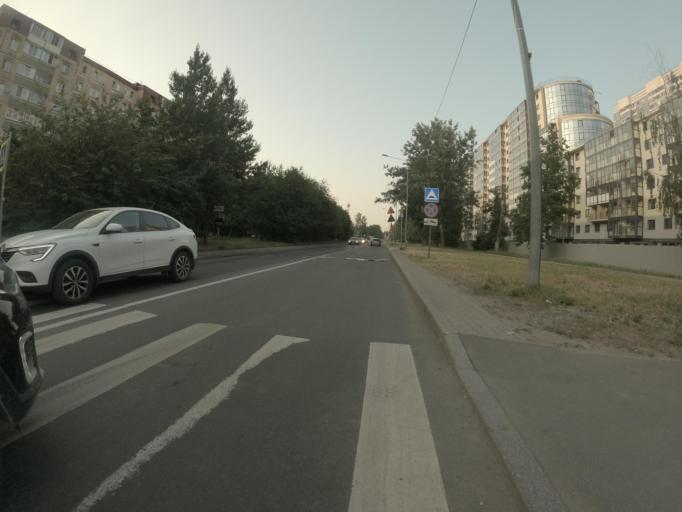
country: RU
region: Leningrad
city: Kalininskiy
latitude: 59.9818
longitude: 30.3858
